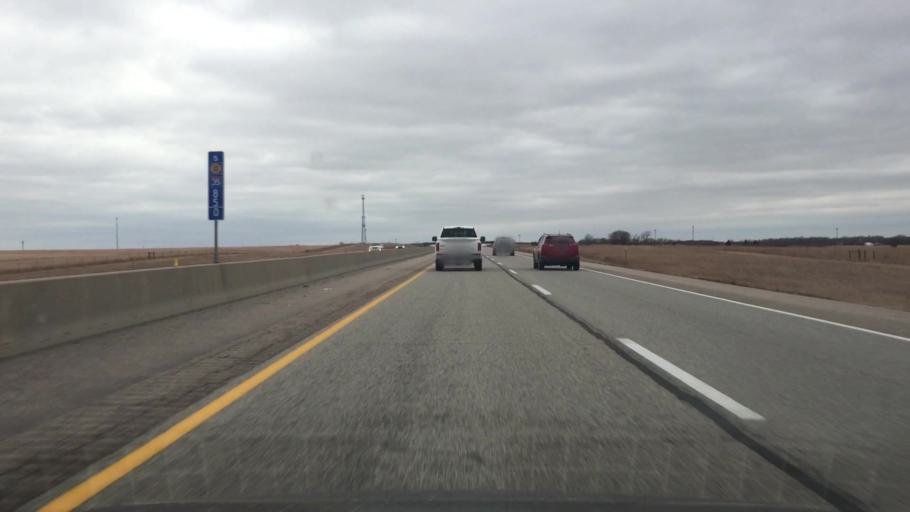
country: US
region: Kansas
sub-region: Butler County
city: El Dorado
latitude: 37.9665
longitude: -96.7262
